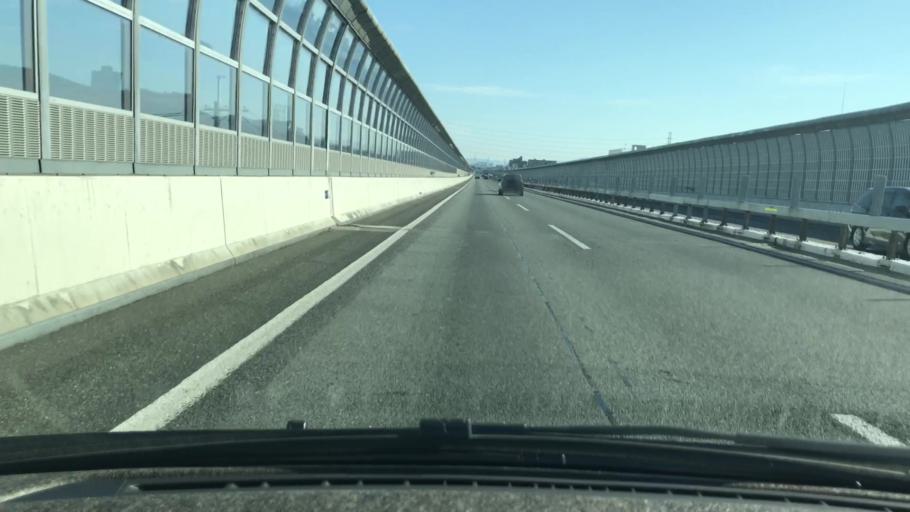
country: JP
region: Hyogo
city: Itami
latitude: 34.7445
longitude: 135.3796
